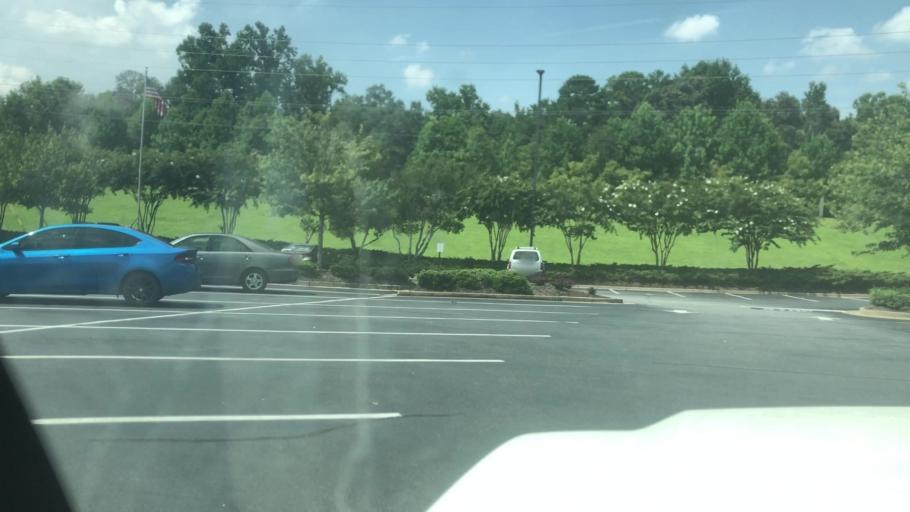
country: US
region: Georgia
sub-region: Jackson County
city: Braselton
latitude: 34.1029
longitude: -83.8134
